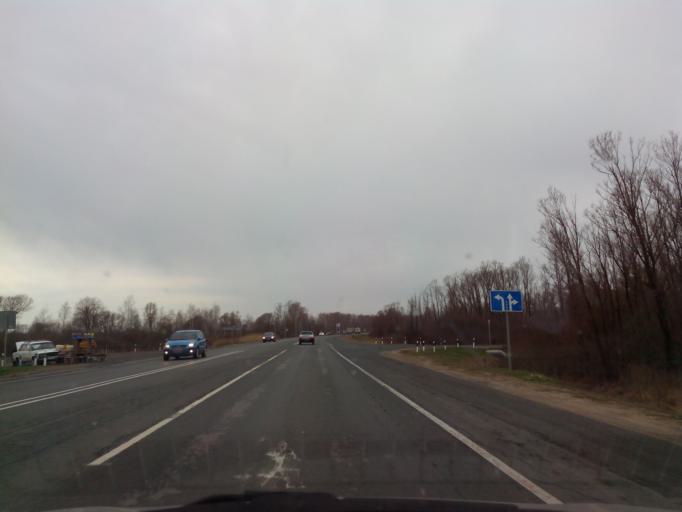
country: RU
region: Tambov
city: Michurinsk
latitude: 53.0833
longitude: 40.4076
